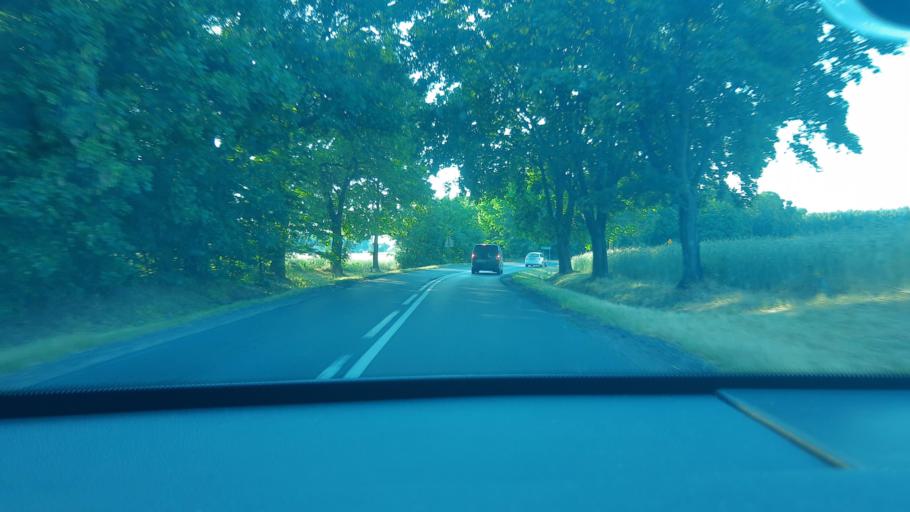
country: PL
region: Lodz Voivodeship
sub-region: Powiat sieradzki
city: Sieradz
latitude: 51.5350
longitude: 18.7681
